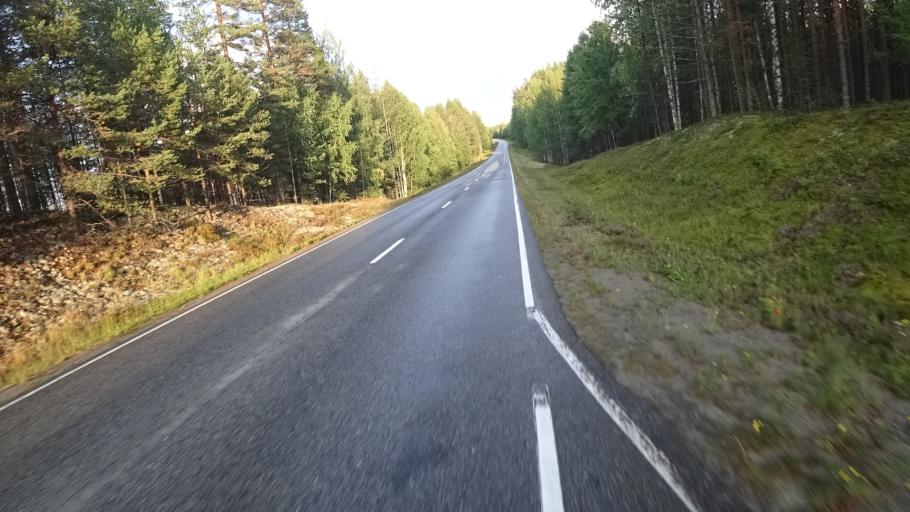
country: FI
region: North Karelia
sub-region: Joensuu
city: Ilomantsi
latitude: 62.6260
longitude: 31.1064
